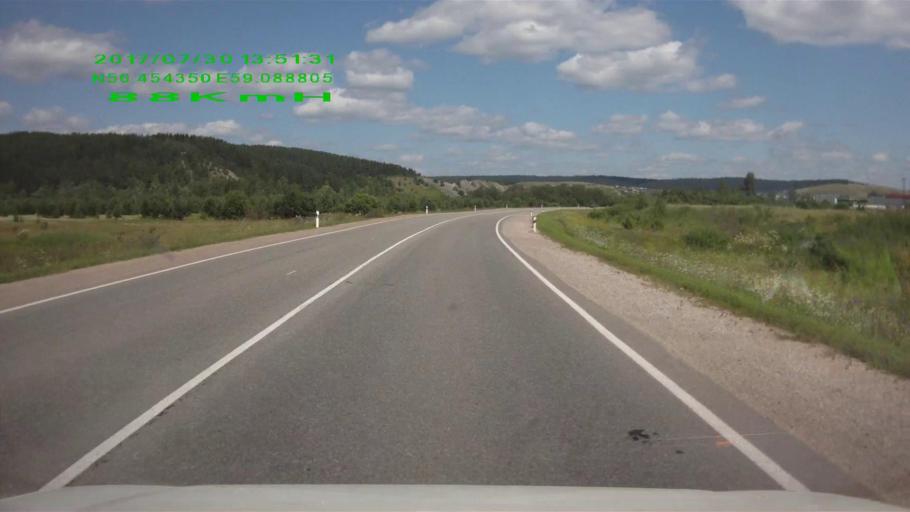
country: RU
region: Sverdlovsk
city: Mikhaylovsk
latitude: 56.4547
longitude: 59.0895
